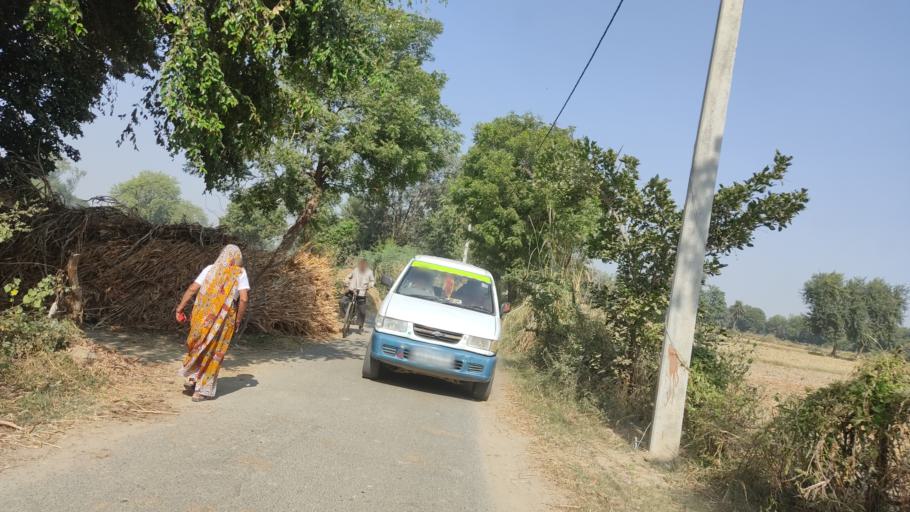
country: IN
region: Uttar Pradesh
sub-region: Mathura
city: Radha Kund
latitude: 27.5125
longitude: 77.4971
